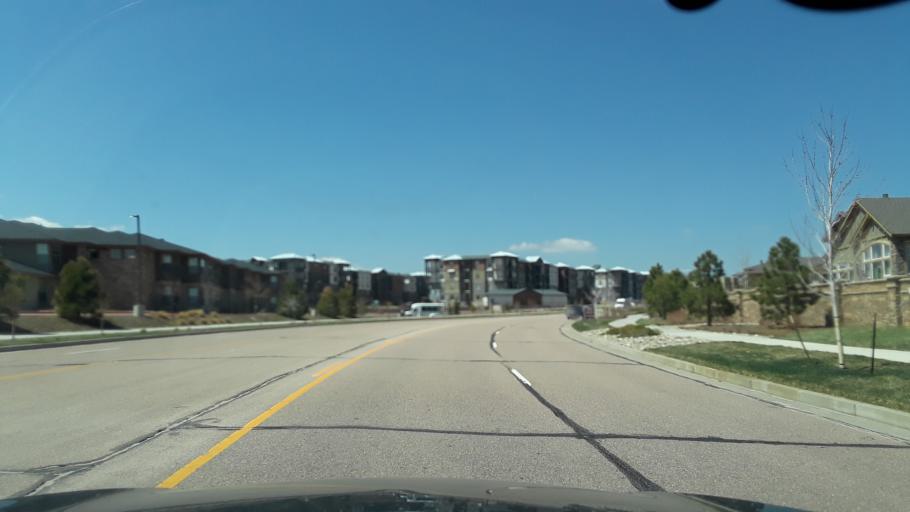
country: US
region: Colorado
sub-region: El Paso County
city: Black Forest
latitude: 38.9618
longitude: -104.7295
